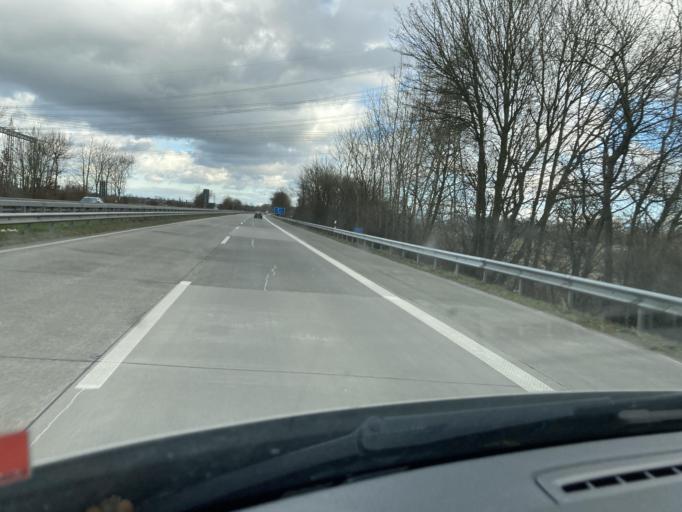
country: DE
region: Lower Saxony
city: Fedderwarden
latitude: 53.5527
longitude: 8.0622
